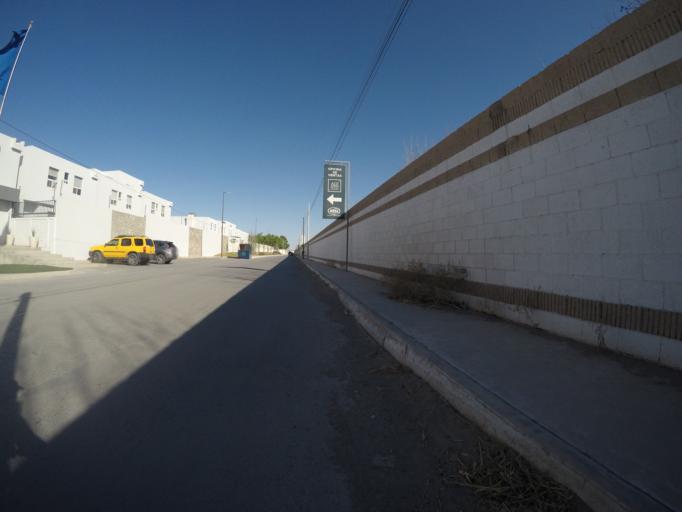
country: MX
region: Chihuahua
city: Ciudad Juarez
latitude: 31.6934
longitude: -106.3973
